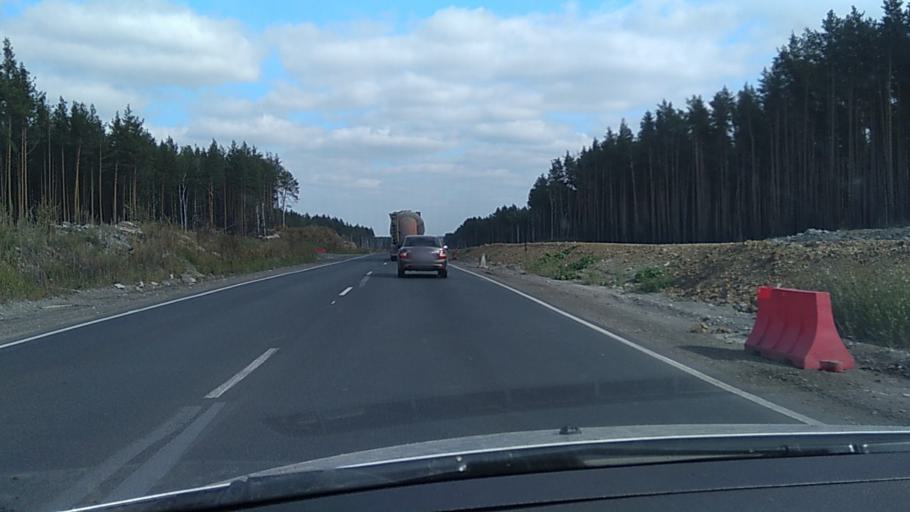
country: RU
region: Chelyabinsk
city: Chebarkul'
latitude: 54.9233
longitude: 60.2607
